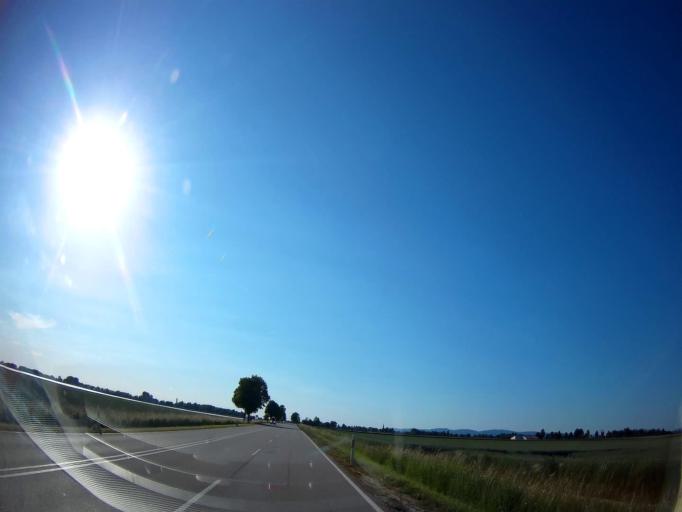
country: DE
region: Bavaria
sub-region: Lower Bavaria
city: Alterhofen
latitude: 48.8286
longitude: 12.6343
